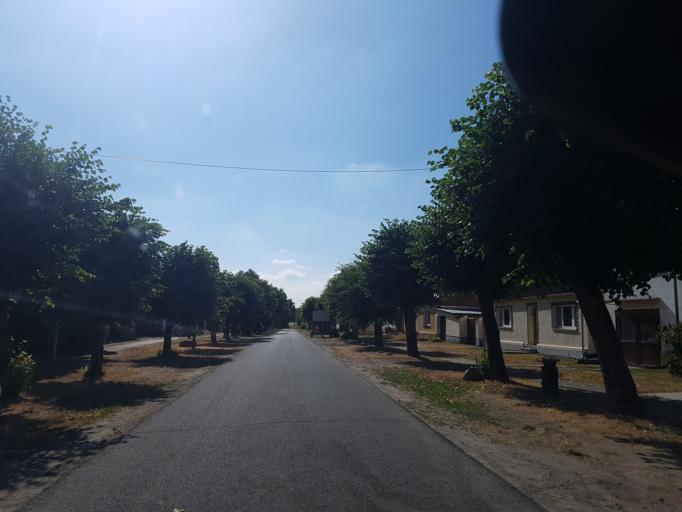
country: DE
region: Brandenburg
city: Treuenbrietzen
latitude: 52.0385
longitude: 12.8671
